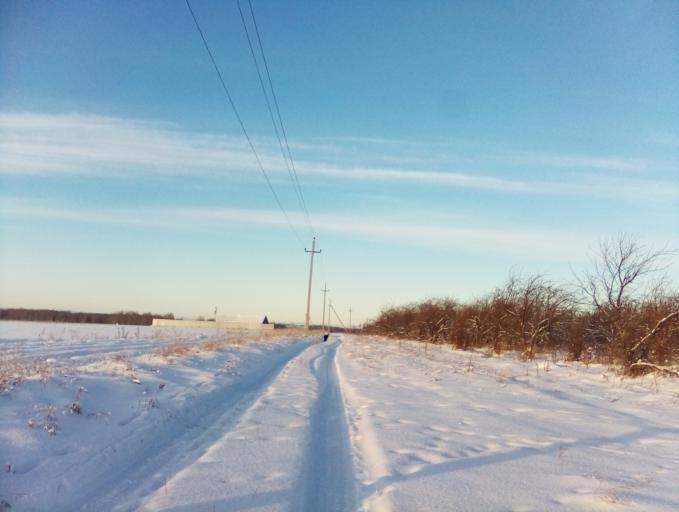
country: RU
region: Chelyabinsk
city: Poletayevo
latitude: 54.9825
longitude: 60.9476
